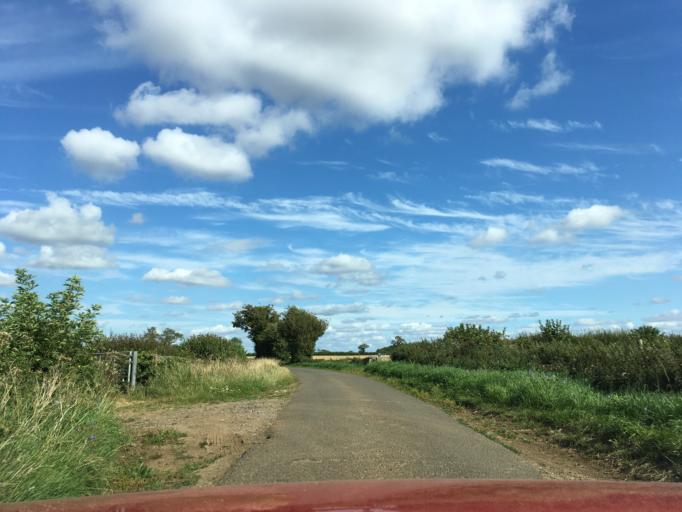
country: GB
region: England
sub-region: Gloucestershire
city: Chalford
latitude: 51.6958
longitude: -2.0966
